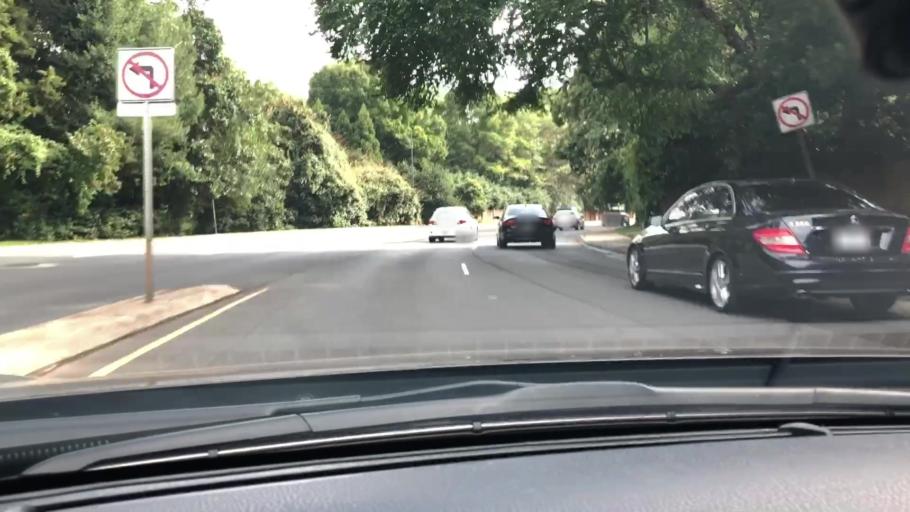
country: US
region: North Carolina
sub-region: Mecklenburg County
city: Charlotte
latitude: 35.1595
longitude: -80.8211
